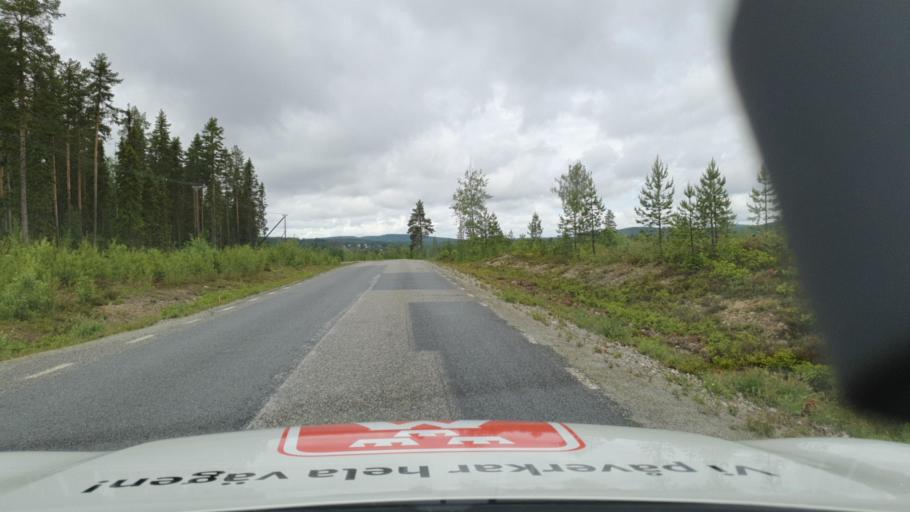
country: SE
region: Vaesterbotten
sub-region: Dorotea Kommun
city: Dorotea
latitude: 64.1646
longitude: 16.6513
